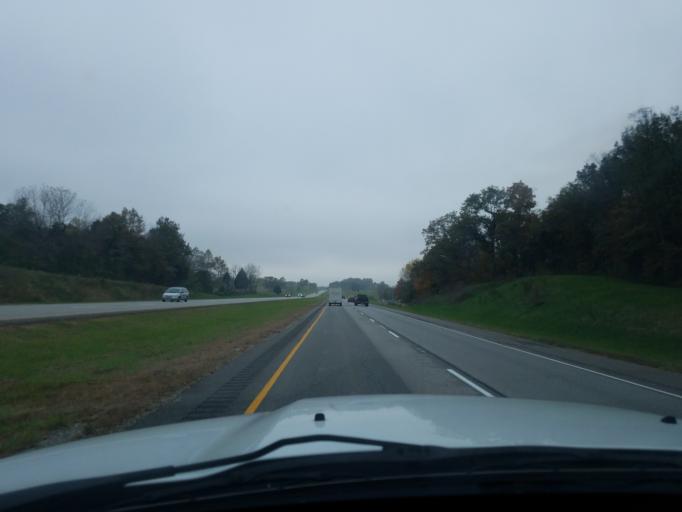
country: US
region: Kentucky
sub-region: Hardin County
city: Elizabethtown
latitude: 37.6219
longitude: -85.8129
